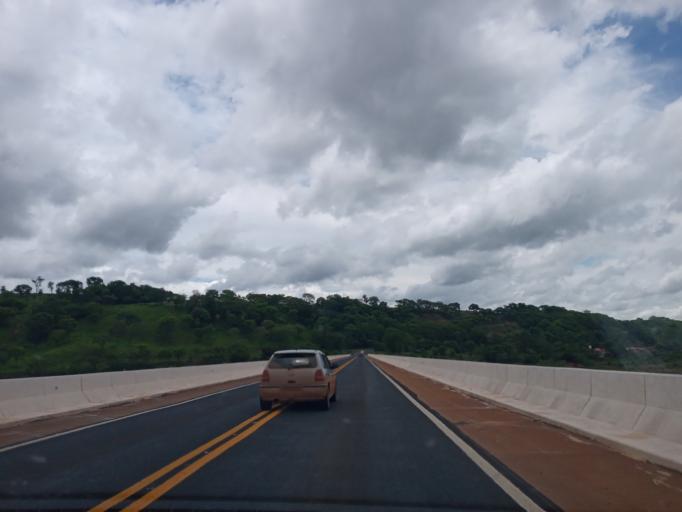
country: BR
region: Minas Gerais
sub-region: Monte Carmelo
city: Monte Carmelo
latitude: -19.2679
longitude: -47.6396
